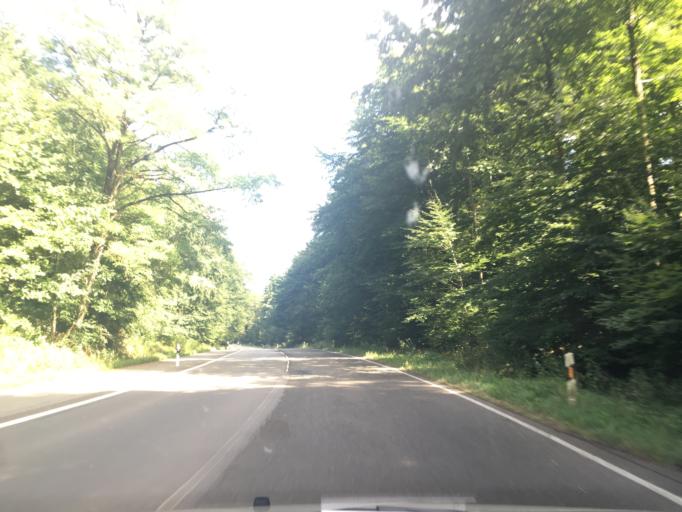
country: DE
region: Saarland
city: Sulzbach
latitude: 49.2757
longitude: 7.0749
